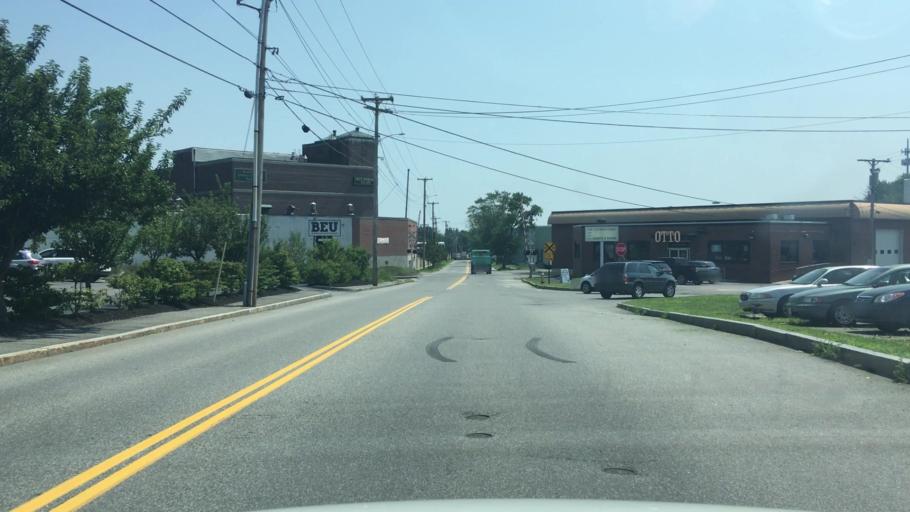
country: US
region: Maine
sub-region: Cumberland County
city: Portland
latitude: 43.6843
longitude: -70.2897
